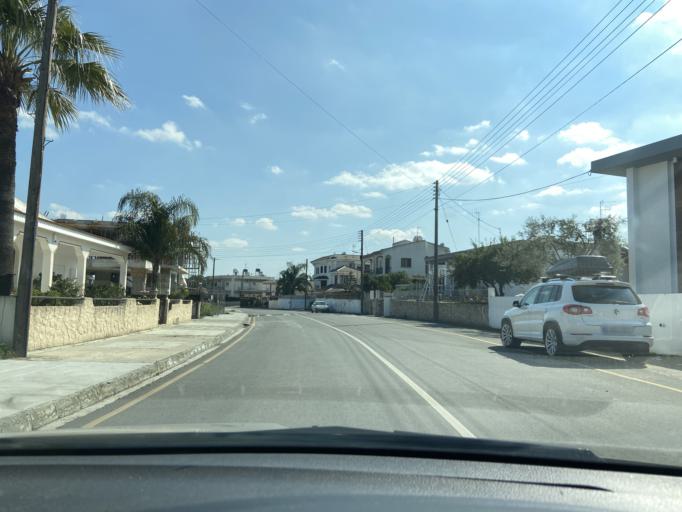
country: CY
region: Lefkosia
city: Alampra
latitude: 35.0210
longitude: 33.3875
